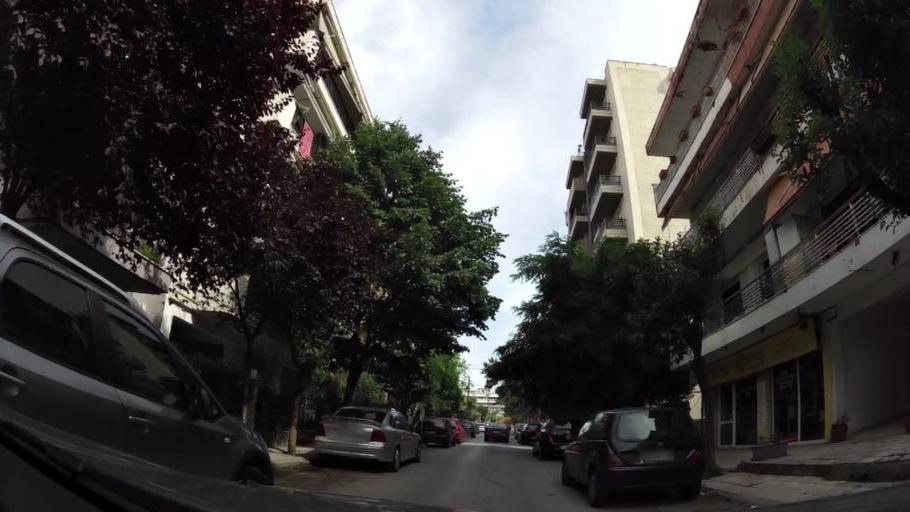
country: GR
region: Central Macedonia
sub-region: Nomos Thessalonikis
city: Kalamaria
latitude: 40.5821
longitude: 22.9472
